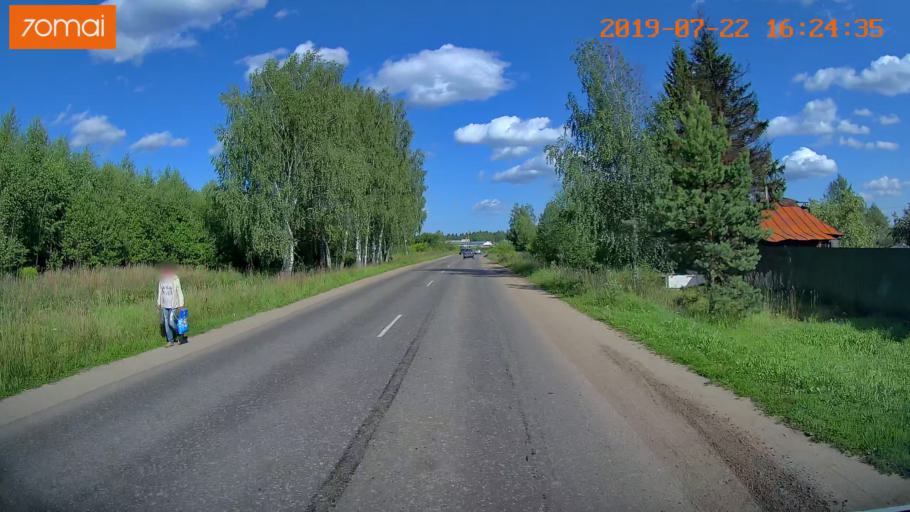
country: RU
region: Ivanovo
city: Novo-Talitsy
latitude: 57.0577
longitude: 40.9160
